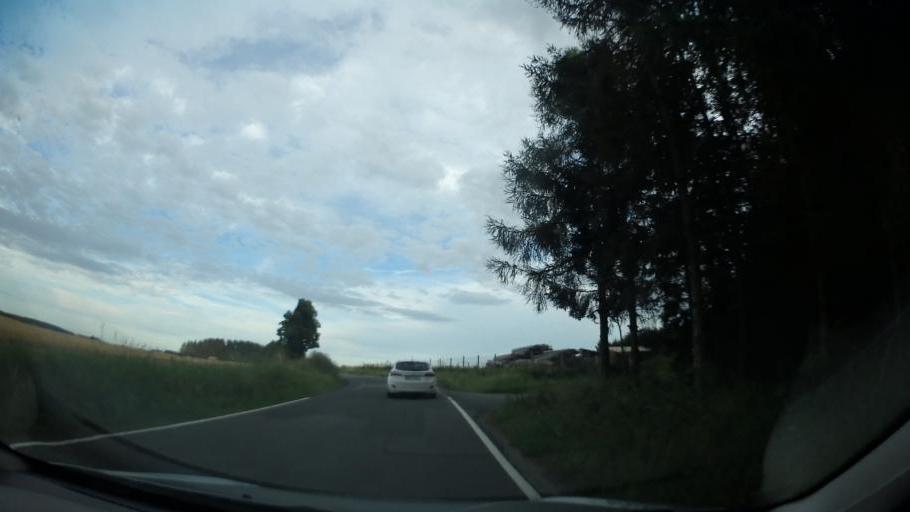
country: CZ
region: Olomoucky
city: Horni Stepanov
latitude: 49.5555
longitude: 16.7706
